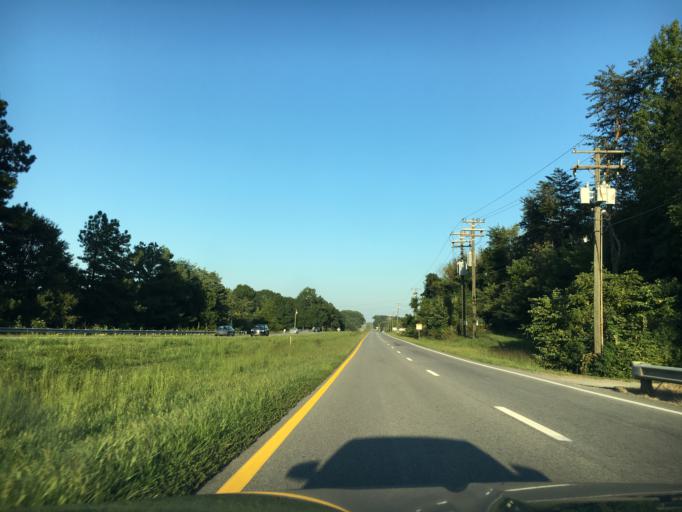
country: US
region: Virginia
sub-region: City of Danville
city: Danville
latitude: 36.5808
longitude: -79.3009
